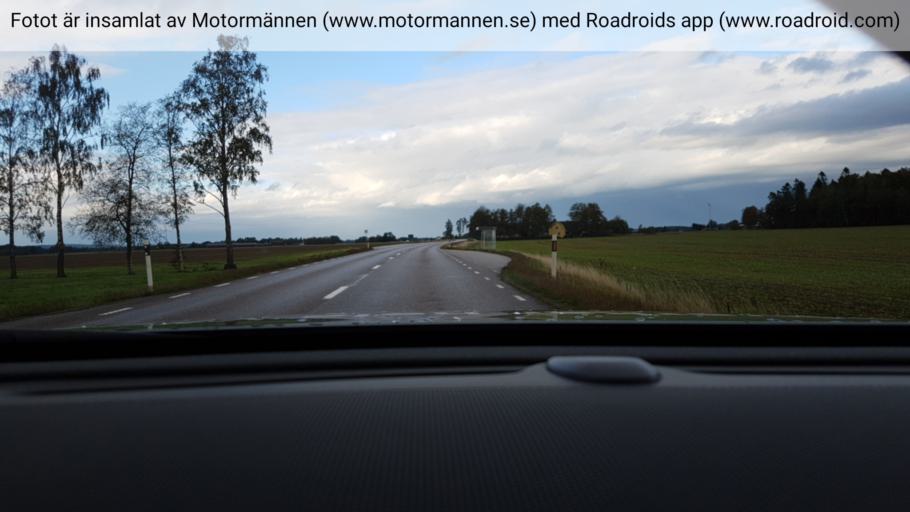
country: SE
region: Vaestra Goetaland
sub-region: Vanersborgs Kommun
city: Bralanda
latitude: 58.6152
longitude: 12.4153
